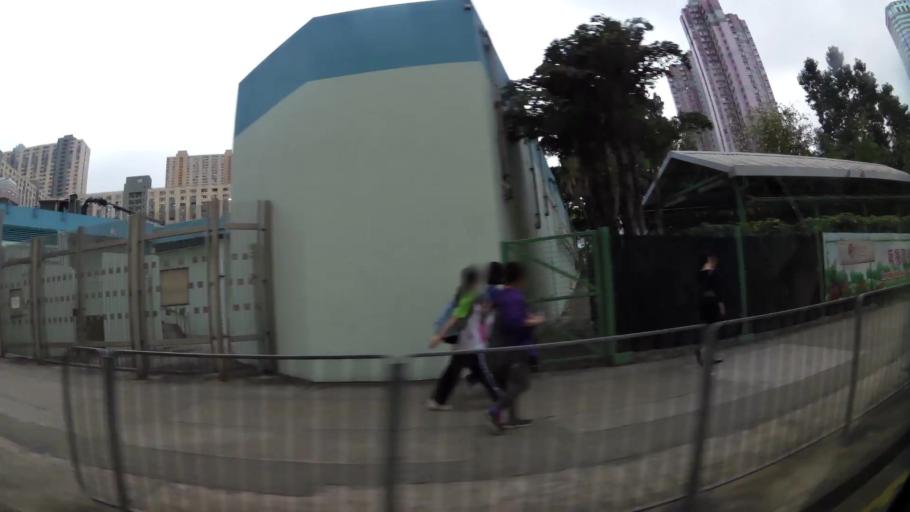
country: HK
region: Tsuen Wan
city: Tsuen Wan
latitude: 22.3583
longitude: 114.1232
